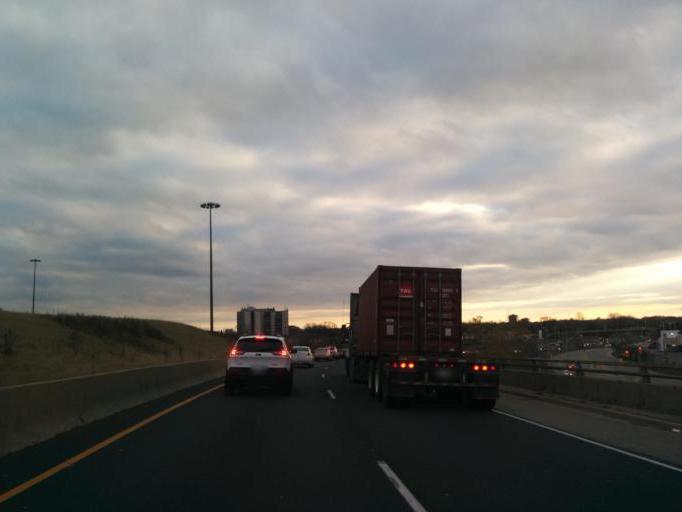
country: CA
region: Ontario
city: Etobicoke
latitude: 43.6144
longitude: -79.5516
